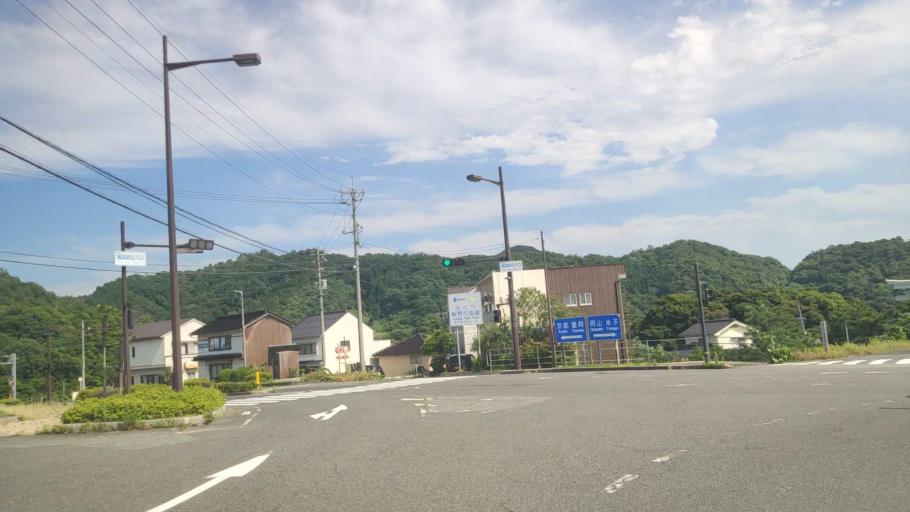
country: JP
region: Tottori
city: Tottori
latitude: 35.5388
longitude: 134.2378
